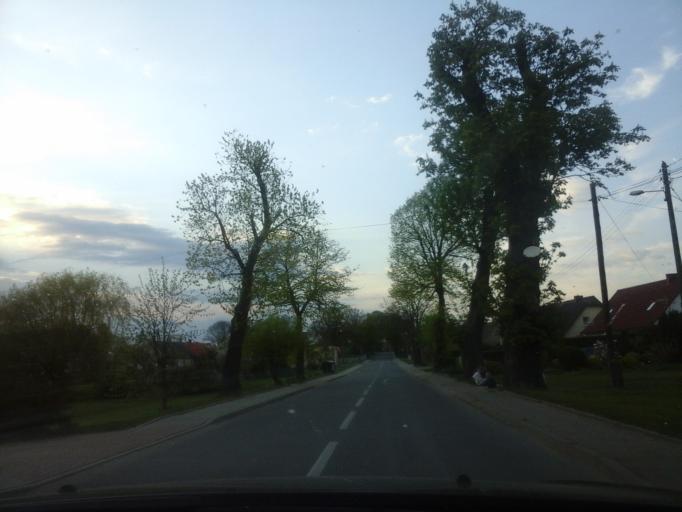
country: PL
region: West Pomeranian Voivodeship
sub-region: Powiat choszczenski
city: Pelczyce
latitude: 53.0190
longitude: 15.3695
